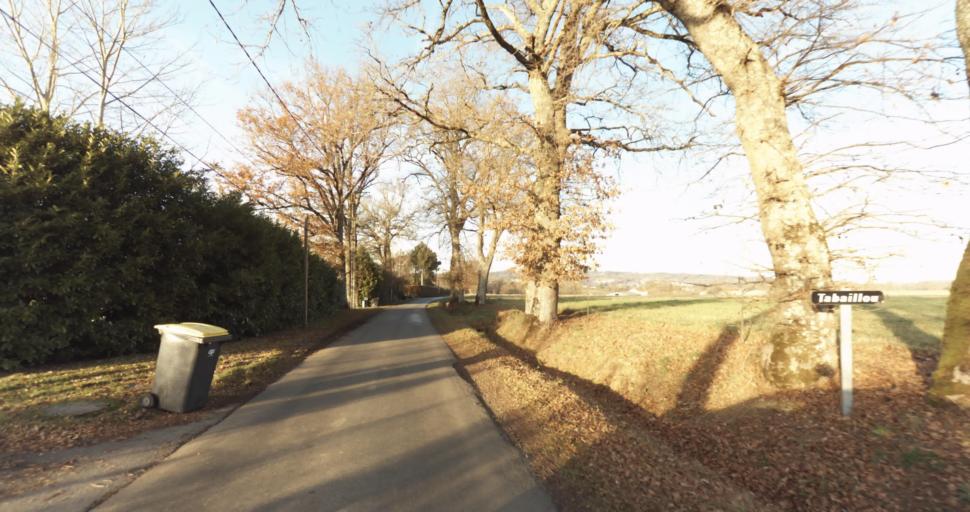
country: FR
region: Limousin
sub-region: Departement de la Haute-Vienne
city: Aixe-sur-Vienne
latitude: 45.7805
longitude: 1.1412
